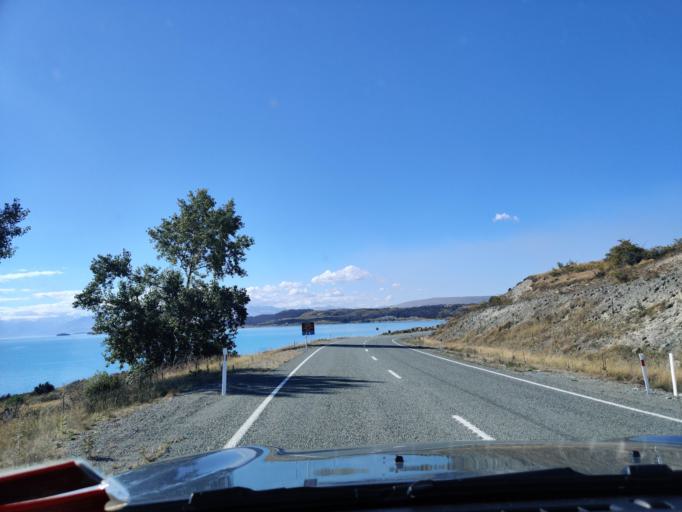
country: NZ
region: Canterbury
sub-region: Timaru District
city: Pleasant Point
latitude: -44.1713
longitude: 170.2063
